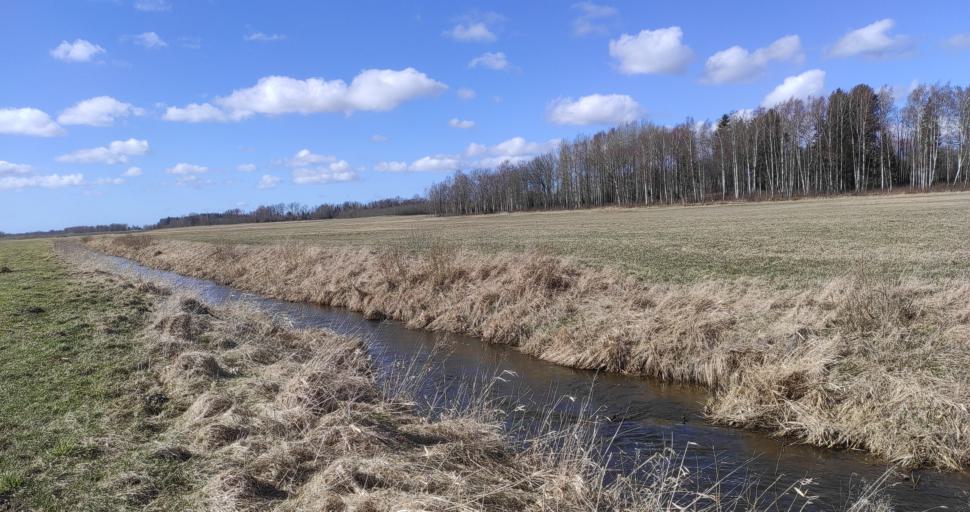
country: LV
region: Aizpute
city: Aizpute
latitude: 56.8464
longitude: 21.7488
